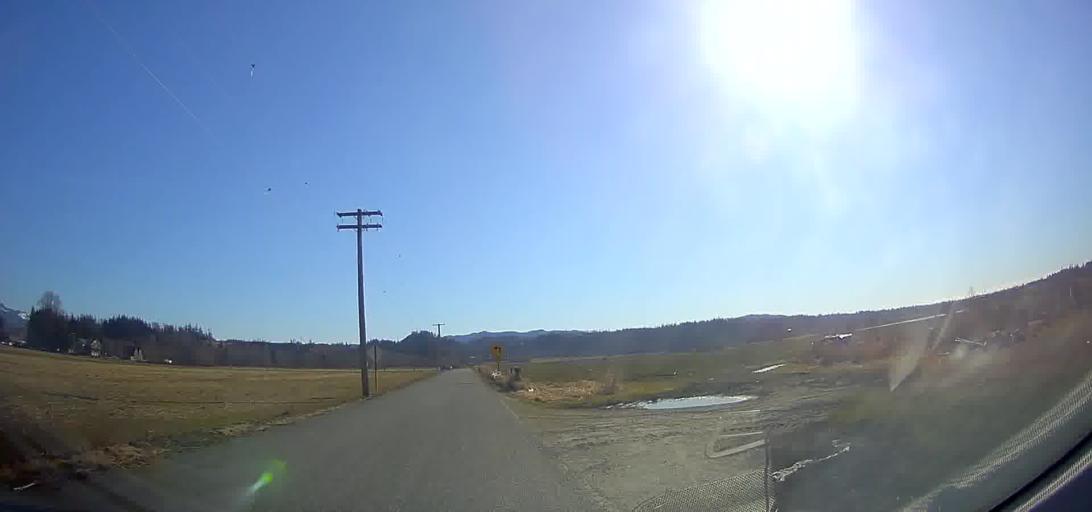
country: US
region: Washington
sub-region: Skagit County
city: Clear Lake
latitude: 48.4511
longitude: -122.2639
